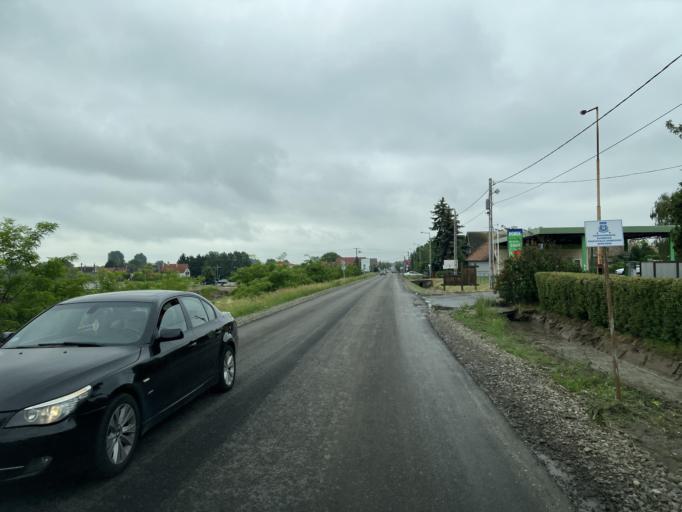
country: HU
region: Pest
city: Galgaheviz
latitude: 47.6175
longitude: 19.5749
